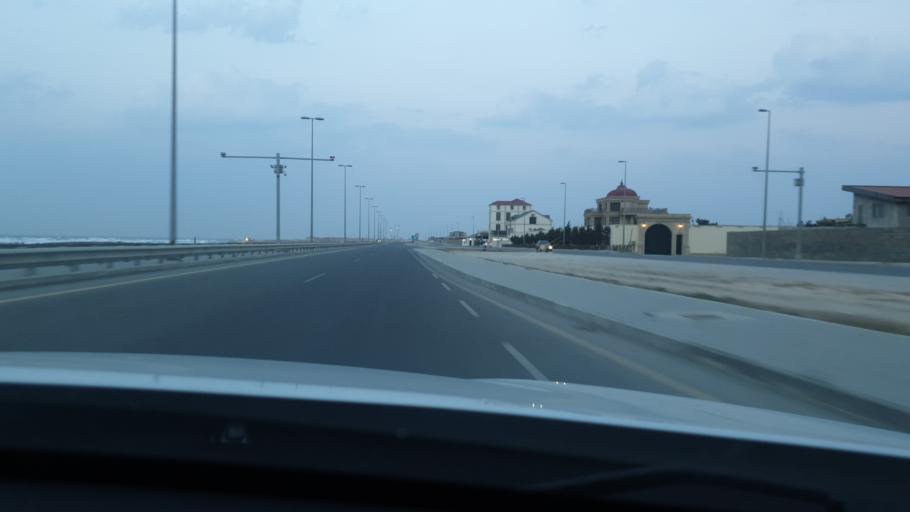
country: AZ
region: Baki
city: Bilajer
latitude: 40.5878
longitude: 50.0437
